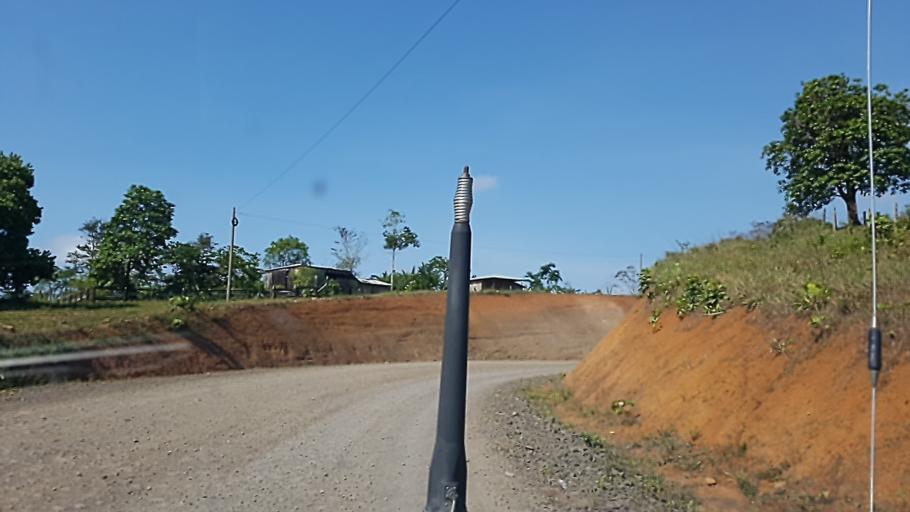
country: NI
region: Atlantico Sur
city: Nueva Guinea
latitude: 11.7846
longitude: -84.1668
